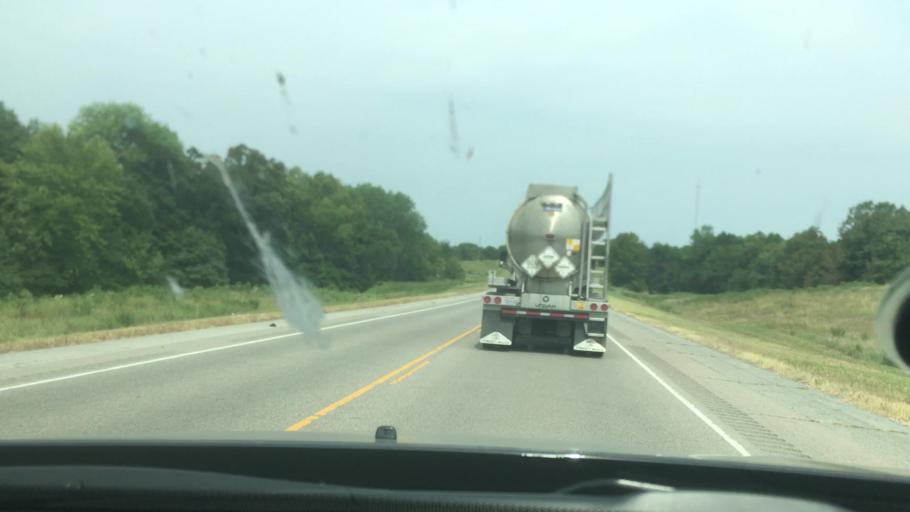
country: US
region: Oklahoma
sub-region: Pontotoc County
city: Ada
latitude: 34.6295
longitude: -96.4676
